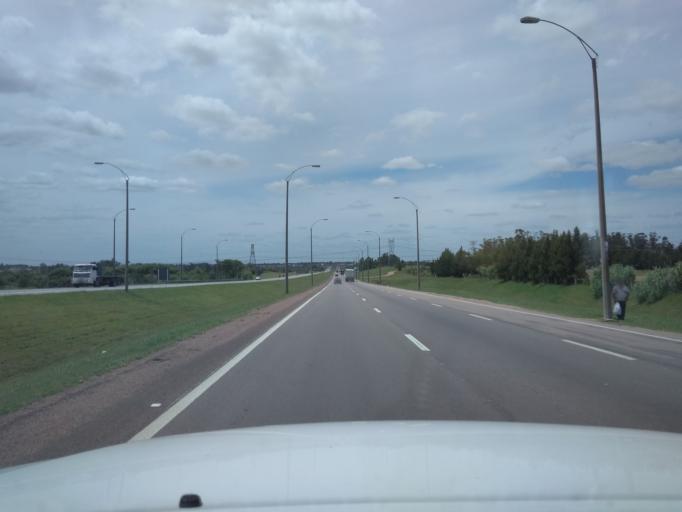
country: UY
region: Canelones
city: La Paz
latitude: -34.7664
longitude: -56.2655
